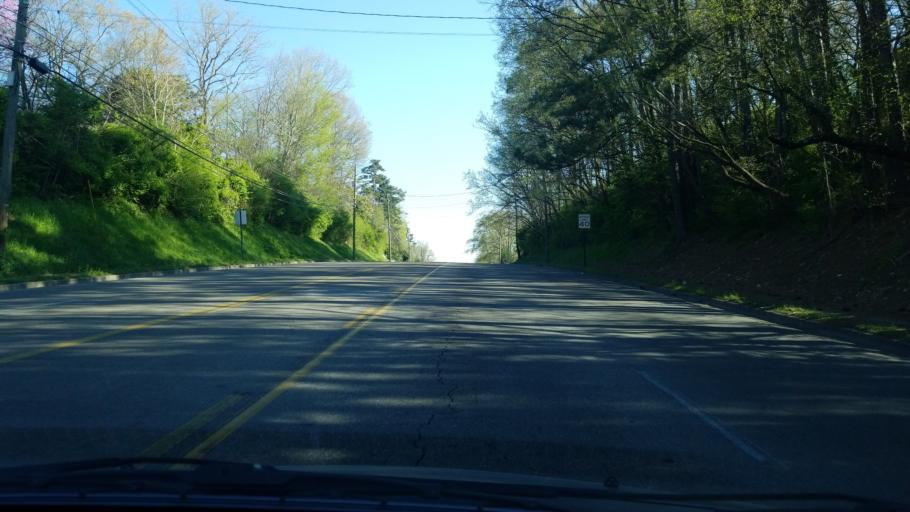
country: US
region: Tennessee
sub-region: Hamilton County
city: East Ridge
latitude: 35.0077
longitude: -85.2554
